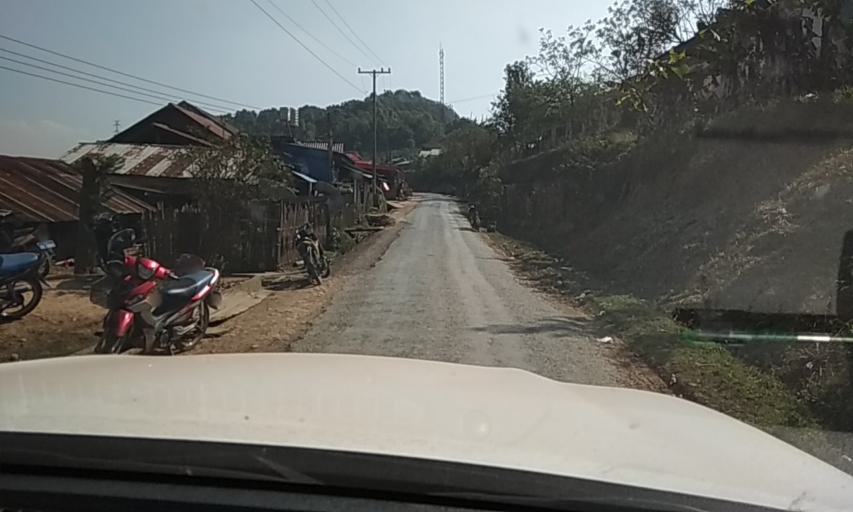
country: LA
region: Phongsali
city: Phongsali
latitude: 21.6651
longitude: 102.0894
